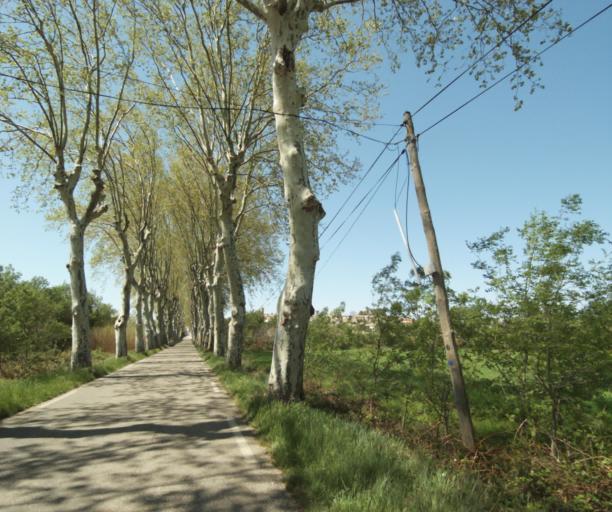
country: FR
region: Languedoc-Roussillon
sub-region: Departement de l'Herault
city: Saint-Genies-des-Mourgues
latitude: 43.6952
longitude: 4.0416
